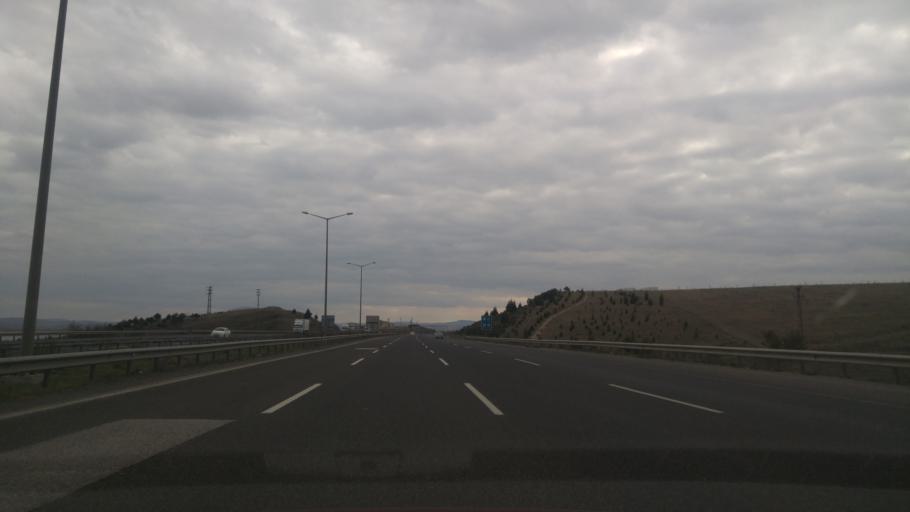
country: TR
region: Ankara
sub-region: Goelbasi
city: Golbasi
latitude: 39.8034
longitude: 32.7930
